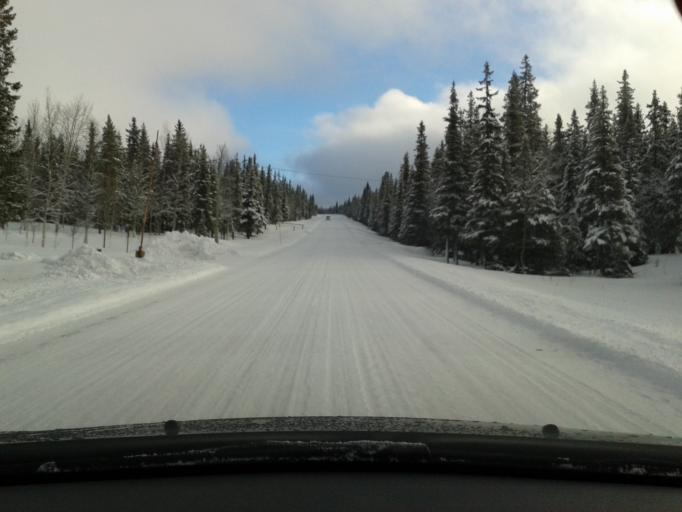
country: SE
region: Vaesterbotten
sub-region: Vilhelmina Kommun
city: Sjoberg
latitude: 65.2511
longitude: 15.6227
